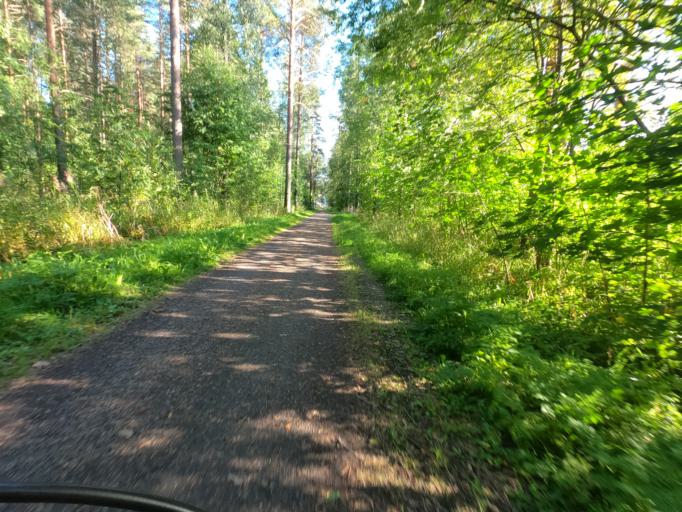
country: FI
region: North Karelia
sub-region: Joensuu
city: Joensuu
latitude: 62.6134
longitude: 29.7585
